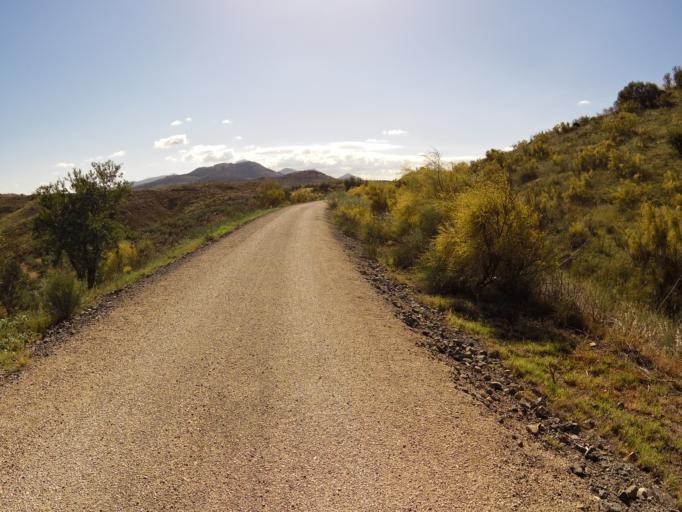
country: ES
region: Andalusia
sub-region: Provincia de Jaen
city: Alcaudete
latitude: 37.5926
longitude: -4.1638
